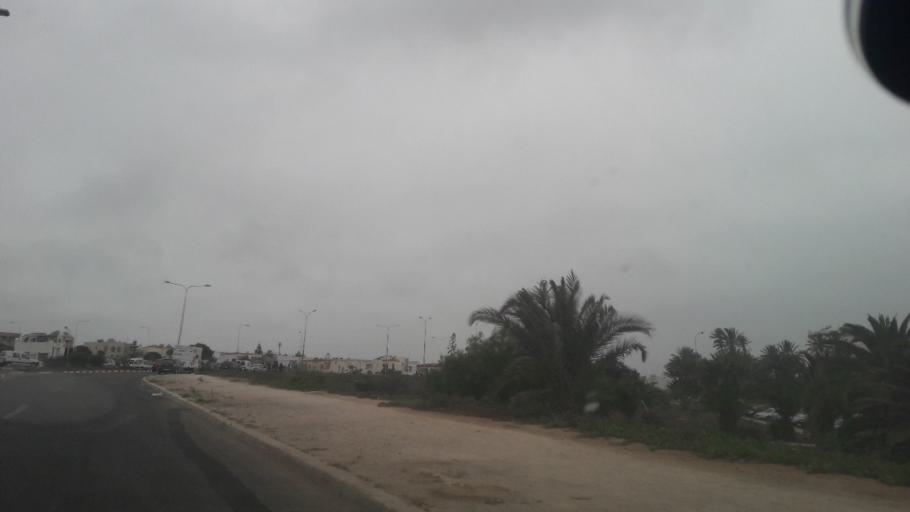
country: MA
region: Souss-Massa-Draa
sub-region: Agadir-Ida-ou-Tnan
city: Agadir
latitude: 30.3970
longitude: -9.5957
